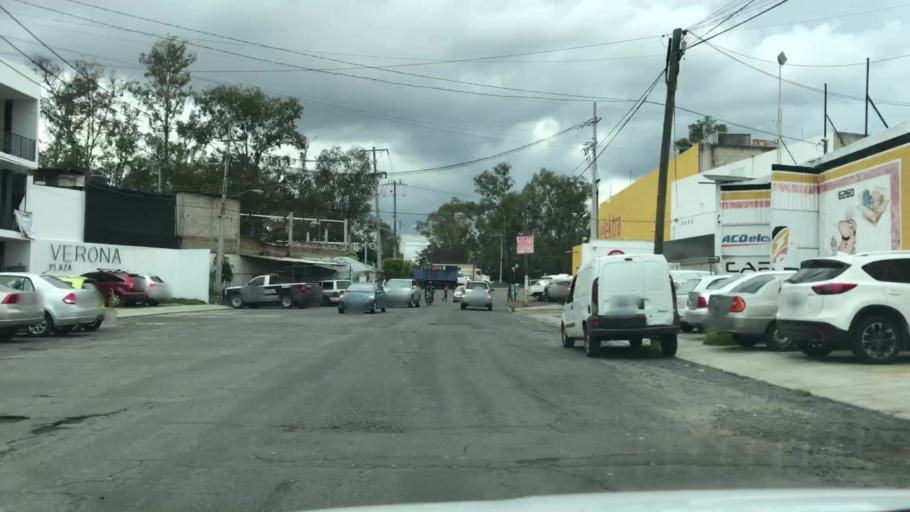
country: MX
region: Jalisco
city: Guadalajara
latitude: 20.6426
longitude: -103.4399
